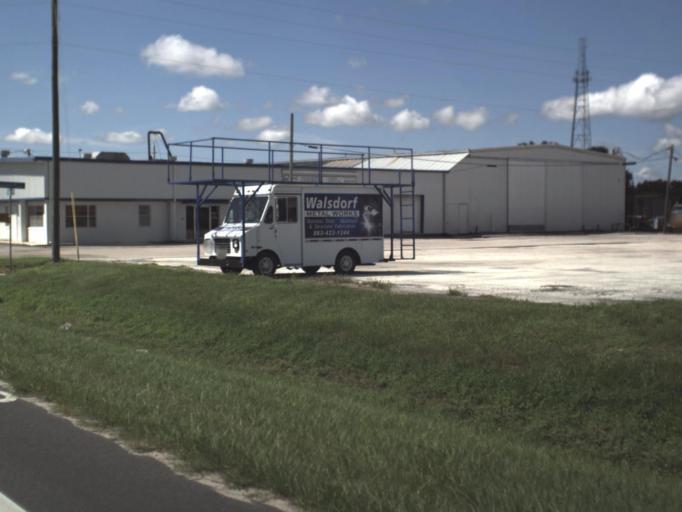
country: US
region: Florida
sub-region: Polk County
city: Haines City
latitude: 28.1092
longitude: -81.6181
